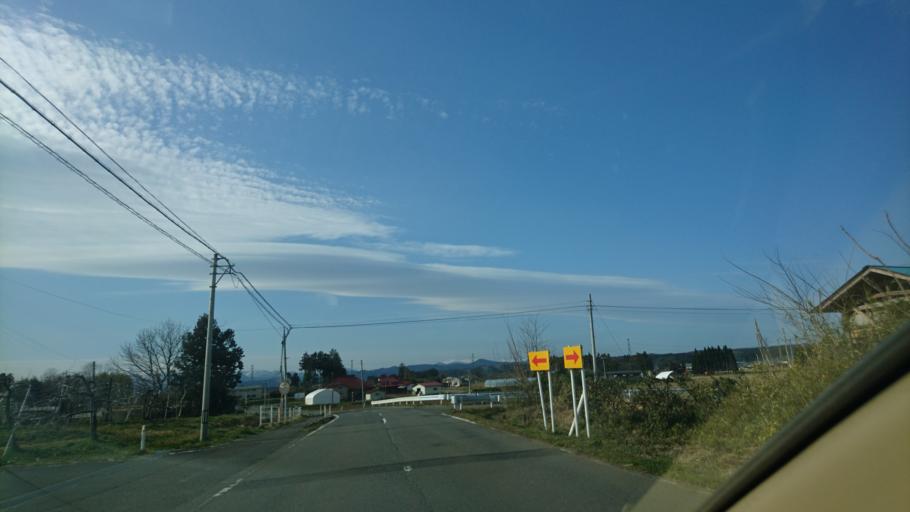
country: JP
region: Iwate
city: Ichinoseki
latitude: 38.8029
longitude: 141.0438
